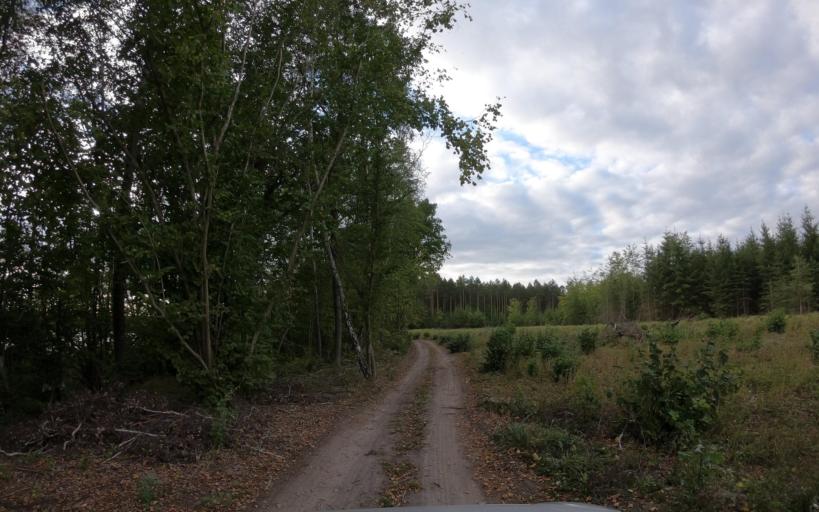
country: PL
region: West Pomeranian Voivodeship
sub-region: Powiat drawski
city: Czaplinek
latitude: 53.5159
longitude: 16.1878
